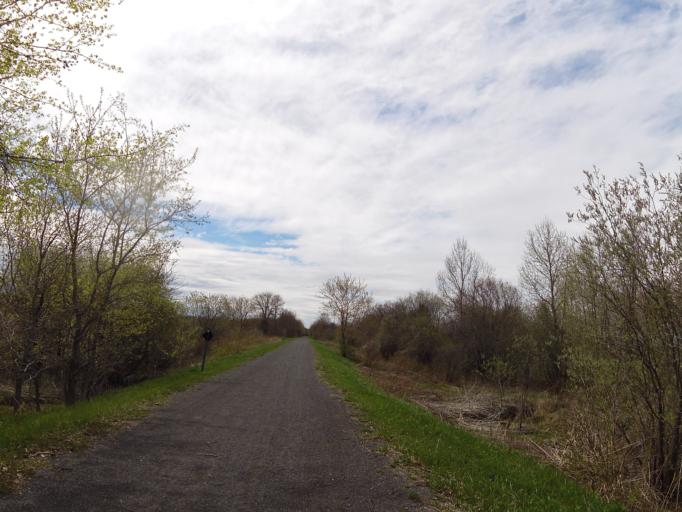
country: CA
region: Ontario
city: Hawkesbury
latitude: 45.5328
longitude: -74.6629
